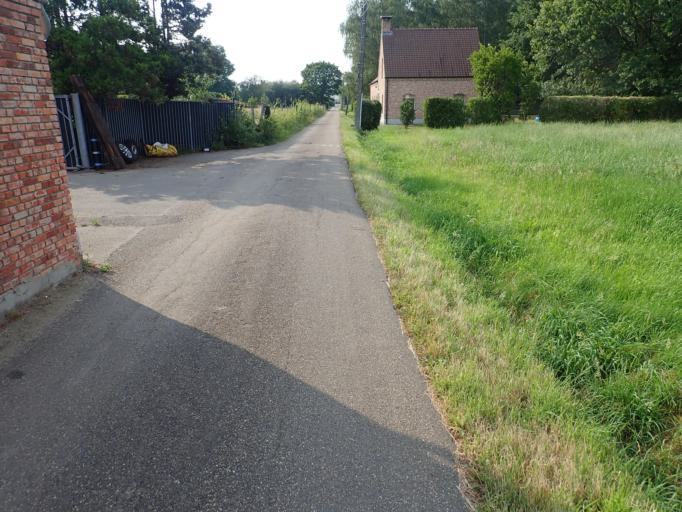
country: BE
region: Flanders
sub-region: Provincie Antwerpen
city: Sint-Katelijne-Waver
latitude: 51.0735
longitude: 4.5690
